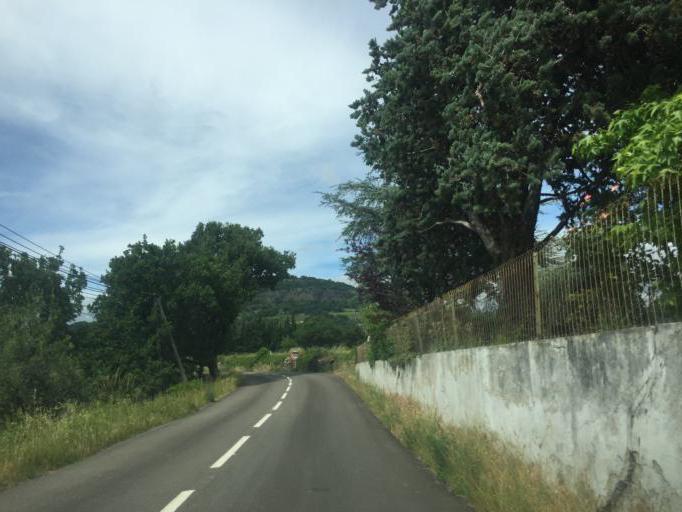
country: FR
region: Rhone-Alpes
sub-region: Departement de l'Ardeche
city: Villeneuve-de-Berg
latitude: 44.5931
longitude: 4.5355
